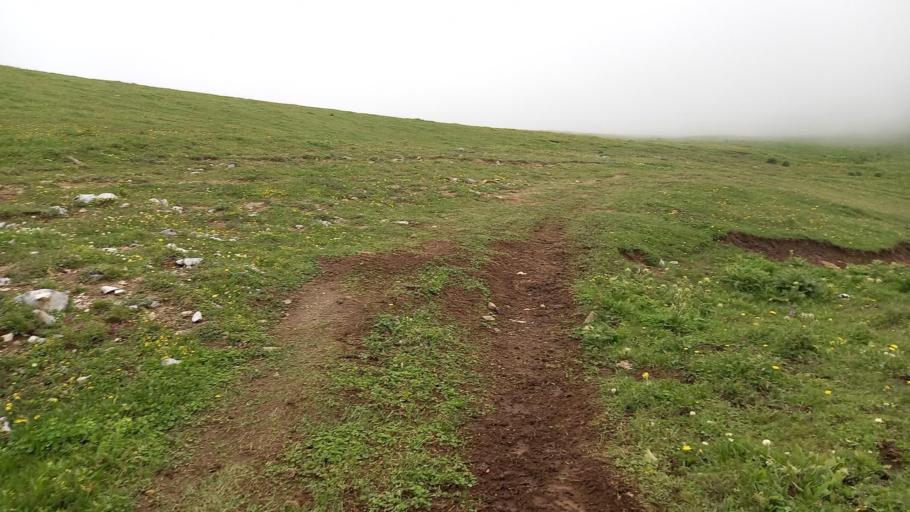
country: RU
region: Karachayevo-Cherkesiya
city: Kurdzhinovo
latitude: 43.7986
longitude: 40.8267
